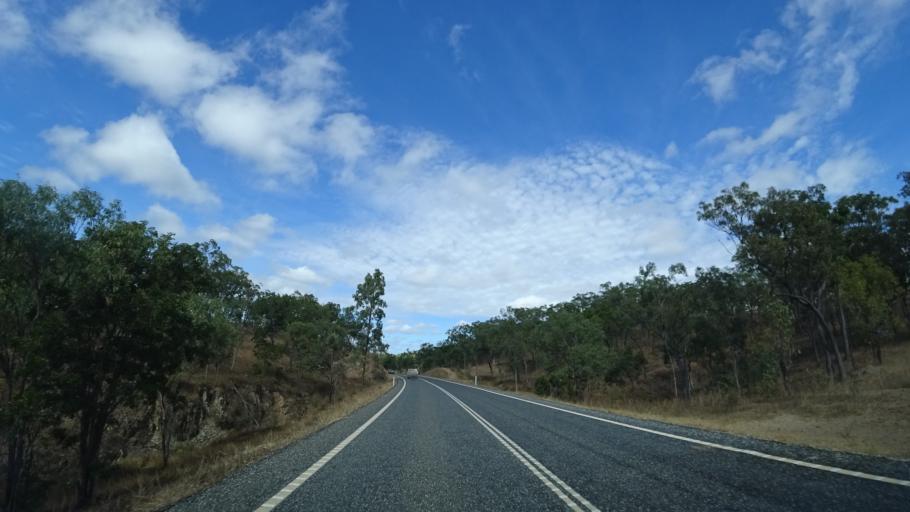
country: AU
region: Queensland
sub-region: Cairns
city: Port Douglas
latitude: -16.2746
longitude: 144.7140
